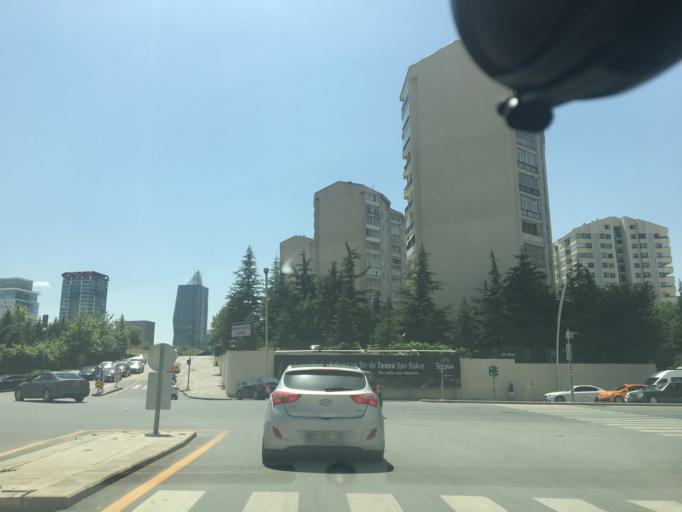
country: TR
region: Ankara
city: Ankara
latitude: 39.9136
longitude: 32.8033
